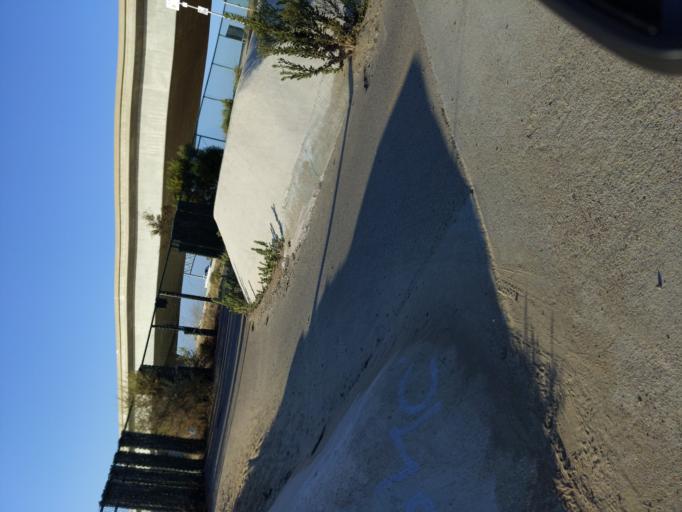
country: US
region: California
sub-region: San Diego County
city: Chula Vista
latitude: 32.6511
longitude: -117.1053
